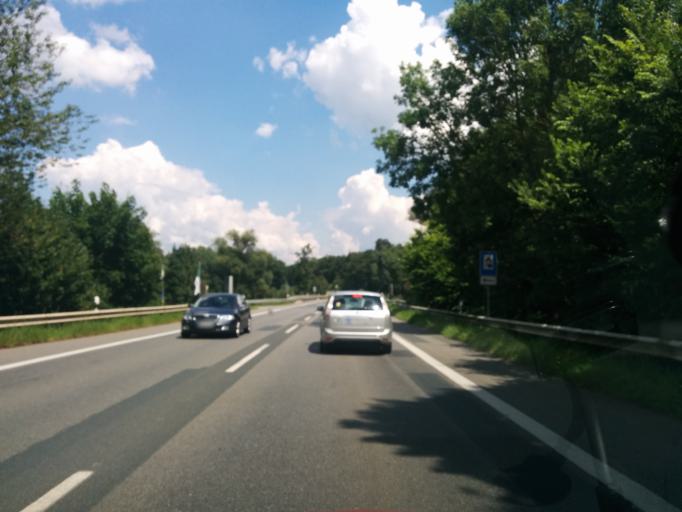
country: DE
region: Lower Saxony
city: Elbingerode
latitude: 51.6273
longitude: 10.2703
